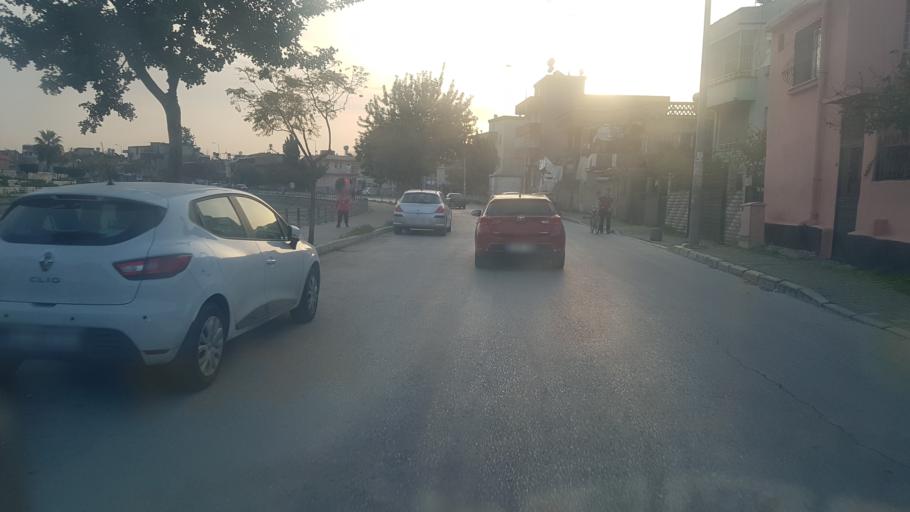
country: TR
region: Adana
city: Adana
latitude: 37.0090
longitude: 35.3259
